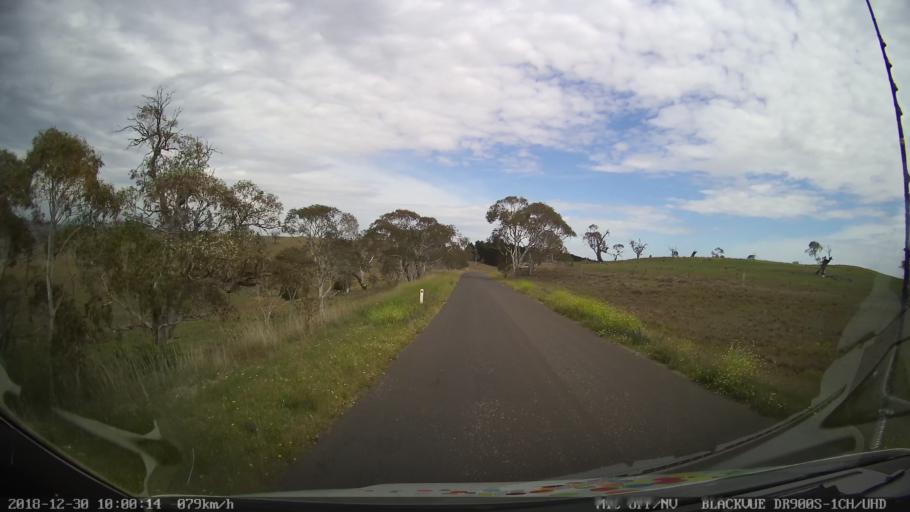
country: AU
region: New South Wales
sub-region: Cooma-Monaro
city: Cooma
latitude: -36.5178
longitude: 149.2006
